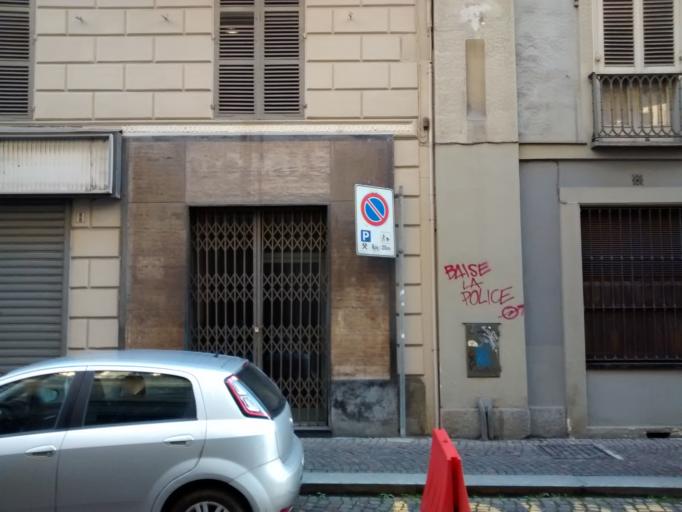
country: IT
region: Piedmont
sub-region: Provincia di Torino
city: Turin
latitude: 45.0738
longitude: 7.6808
